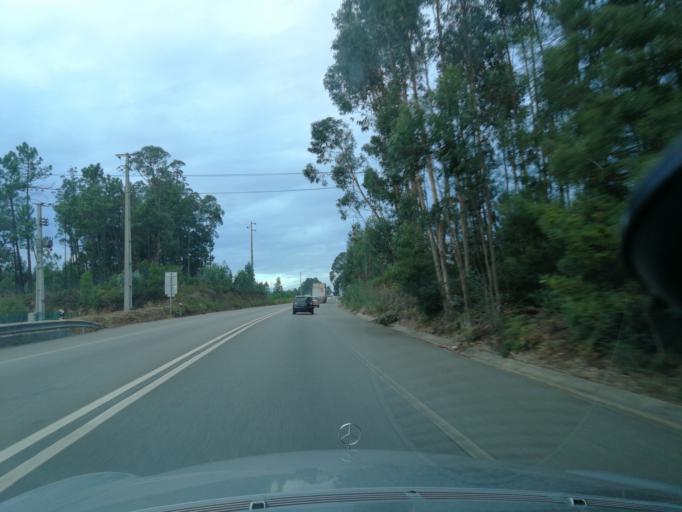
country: PT
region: Aveiro
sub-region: Albergaria-A-Velha
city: Albergaria-a-Velha
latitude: 40.6657
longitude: -8.4754
